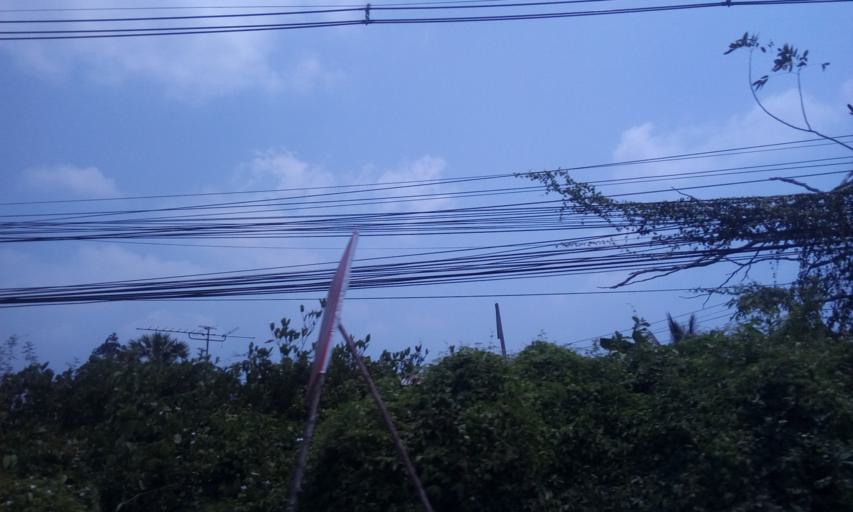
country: TH
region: Chachoengsao
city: Chachoengsao
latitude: 13.7208
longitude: 101.0902
